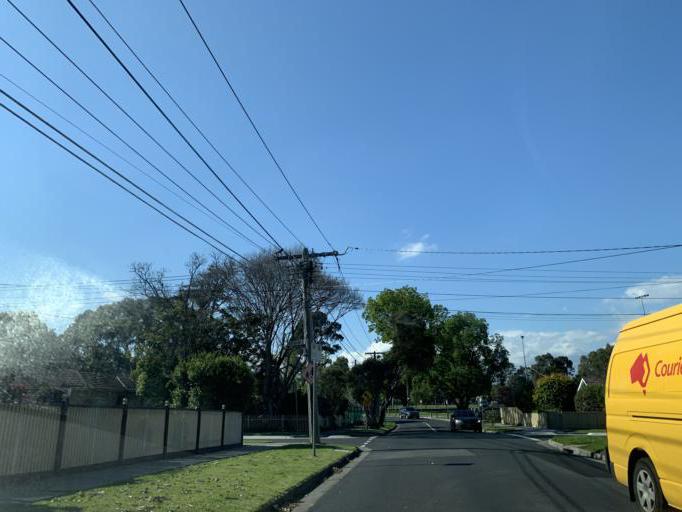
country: AU
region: Victoria
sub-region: Kingston
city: Mordialloc
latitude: -37.9927
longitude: 145.0886
